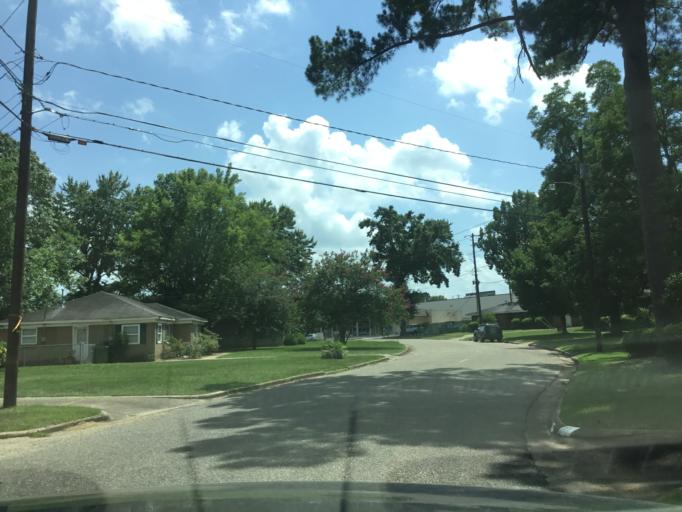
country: US
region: Alabama
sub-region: Montgomery County
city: Montgomery
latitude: 32.3862
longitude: -86.2587
